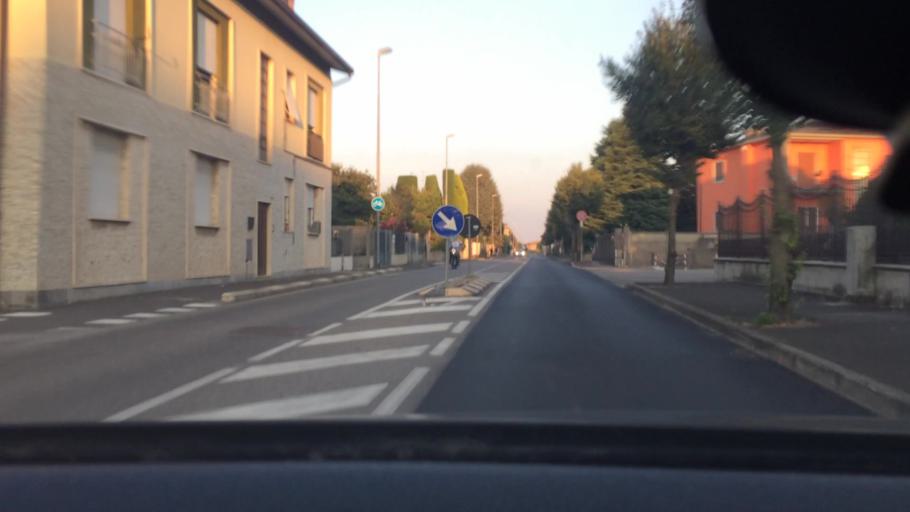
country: IT
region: Lombardy
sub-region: Provincia di Como
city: Rovello Porro
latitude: 45.6495
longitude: 9.0456
